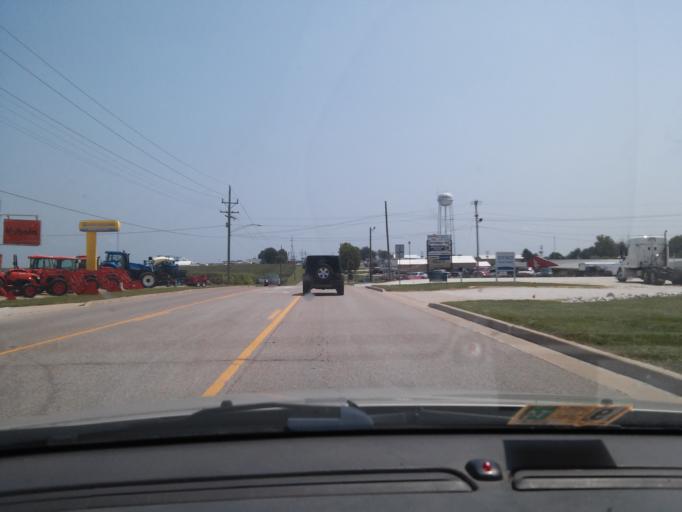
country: US
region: Illinois
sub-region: Pike County
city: Pittsfield
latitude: 39.6047
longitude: -90.8449
